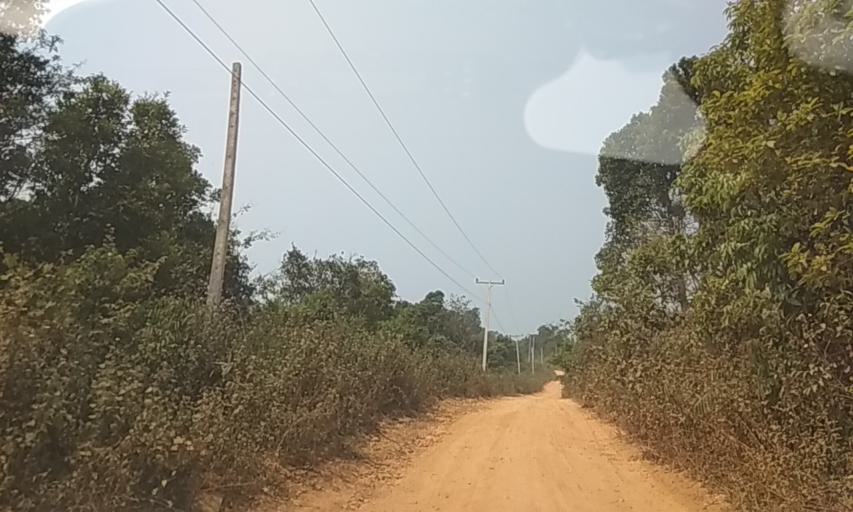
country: TH
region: Nan
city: Chaloem Phra Kiat
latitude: 20.0094
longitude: 101.1267
